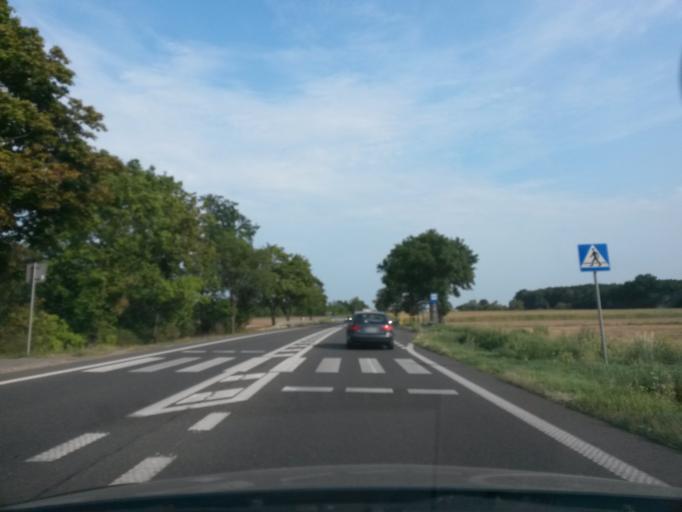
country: PL
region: Masovian Voivodeship
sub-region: Powiat sierpecki
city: Rosciszewo
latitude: 52.8339
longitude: 19.7449
